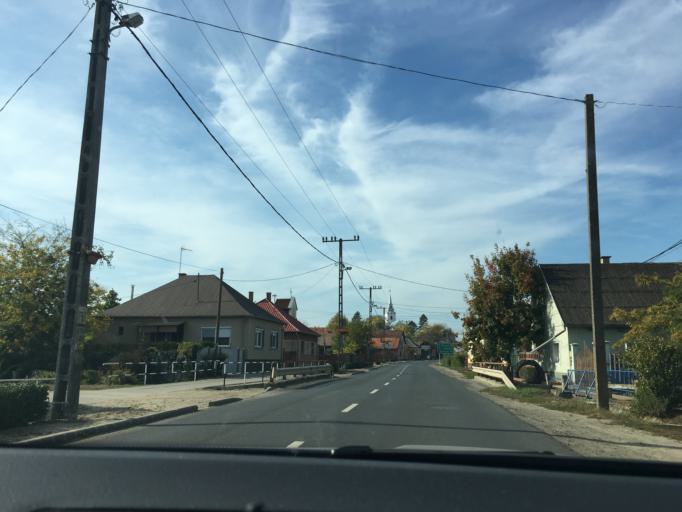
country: HU
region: Hajdu-Bihar
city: Vamospercs
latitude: 47.5247
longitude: 21.9030
